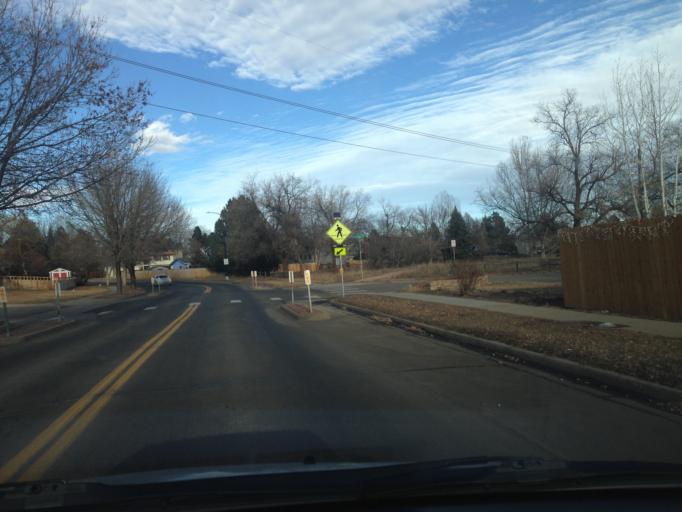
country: US
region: Colorado
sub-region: Boulder County
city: Lafayette
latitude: 39.9902
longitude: -105.1089
